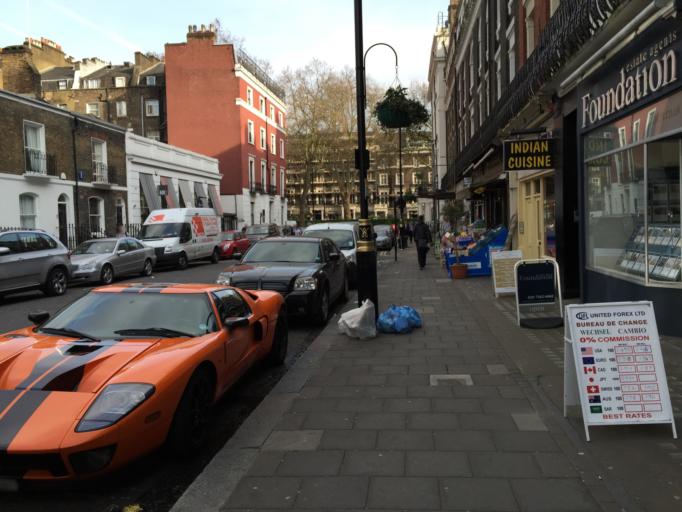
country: GB
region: England
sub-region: Greater London
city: Bayswater
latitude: 51.5147
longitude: -0.1756
